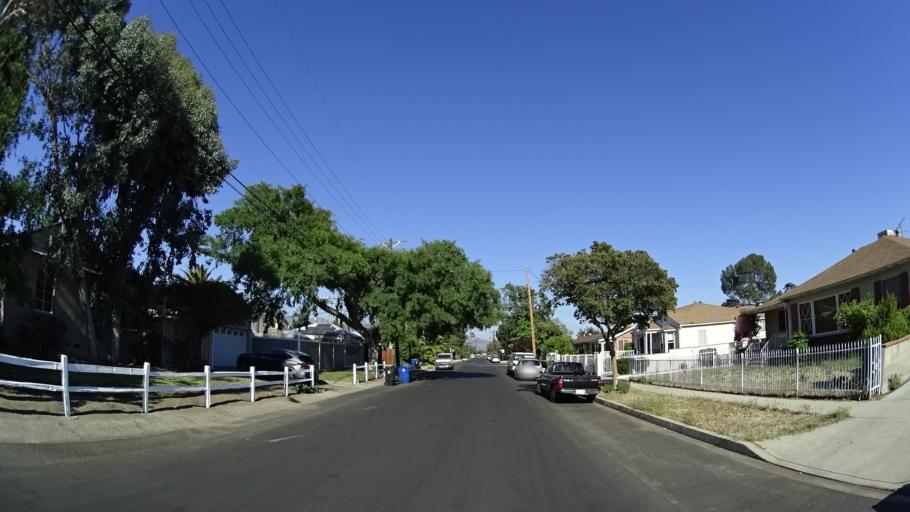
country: US
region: California
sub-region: Los Angeles County
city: North Hollywood
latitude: 34.1830
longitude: -118.3756
